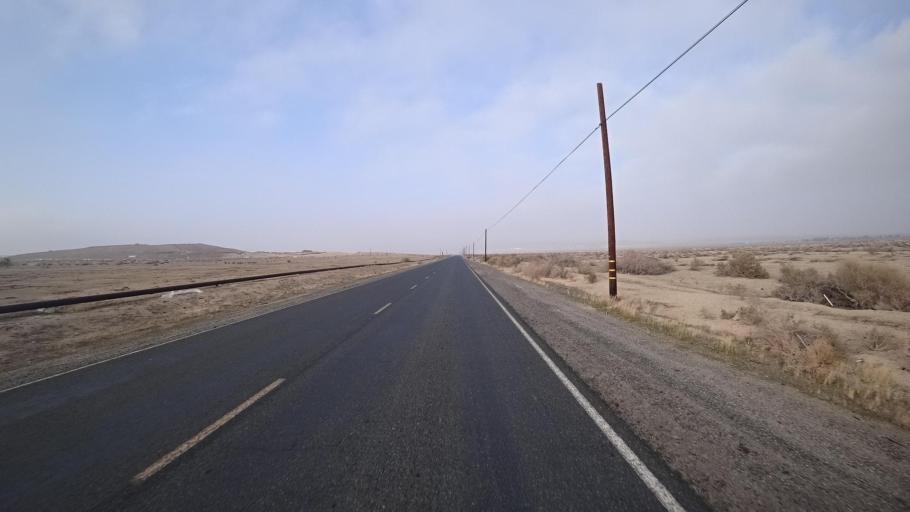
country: US
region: California
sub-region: Kern County
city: Ford City
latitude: 35.1981
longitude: -119.4457
